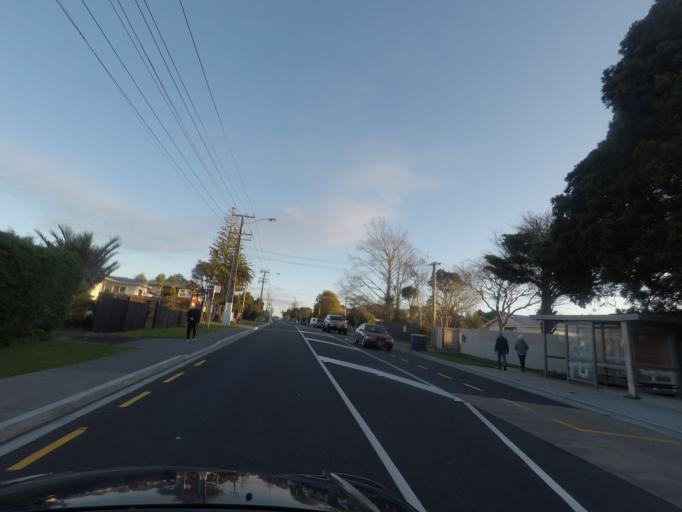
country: NZ
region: Auckland
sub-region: Auckland
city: Rosebank
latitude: -36.8803
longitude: 174.6462
